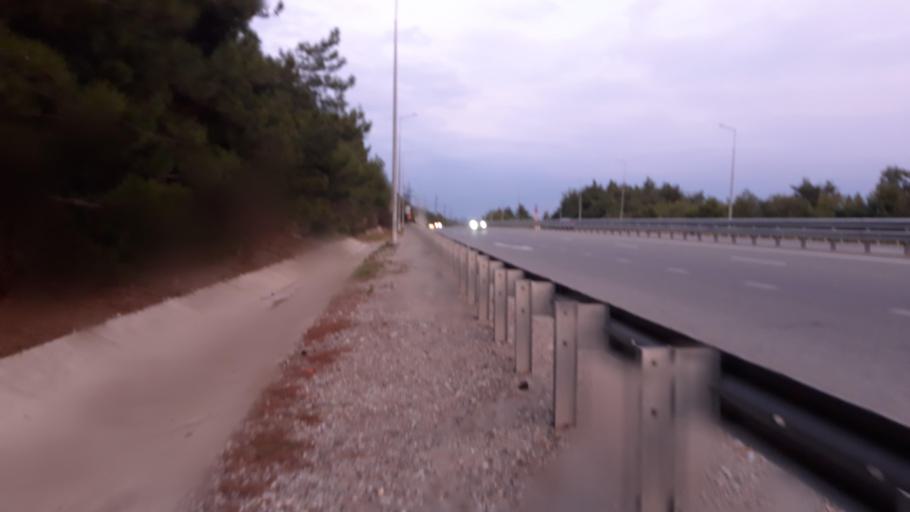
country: RU
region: Krasnodarskiy
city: Gelendzhik
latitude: 44.5783
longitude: 38.0880
